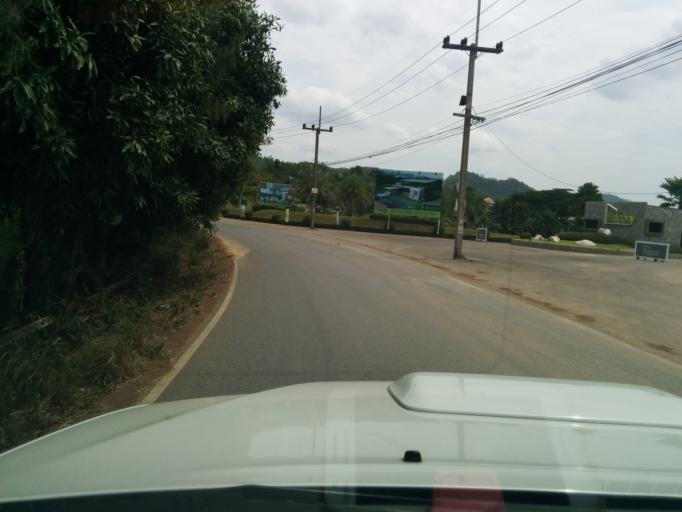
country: TH
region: Sara Buri
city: Muak Lek
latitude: 14.5849
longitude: 101.2260
